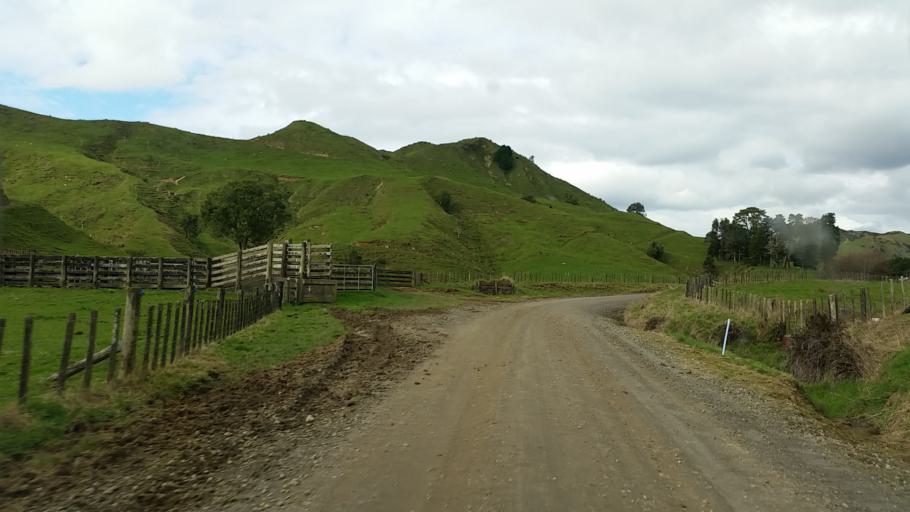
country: NZ
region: Taranaki
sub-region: New Plymouth District
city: Waitara
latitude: -39.1611
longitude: 174.5951
